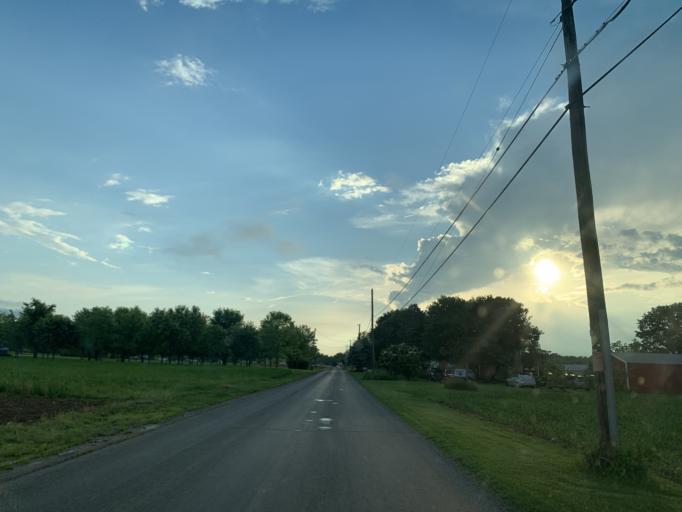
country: US
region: Maryland
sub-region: Cecil County
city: Rising Sun
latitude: 39.7218
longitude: -76.0231
